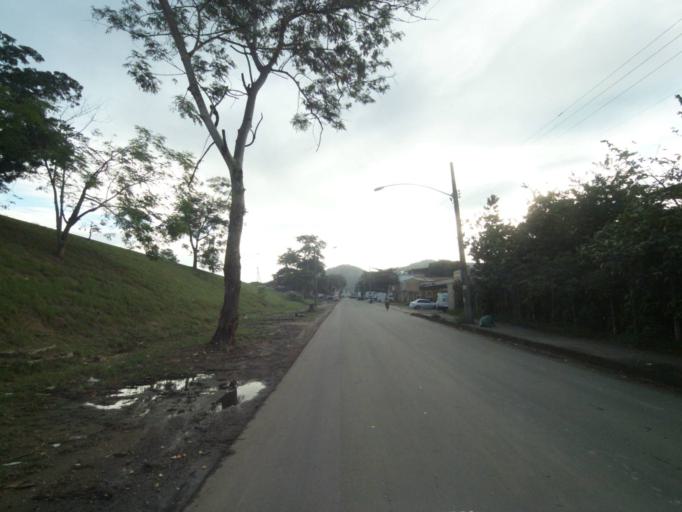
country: BR
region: Rio de Janeiro
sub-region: Nilopolis
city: Nilopolis
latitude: -22.8555
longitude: -43.4799
